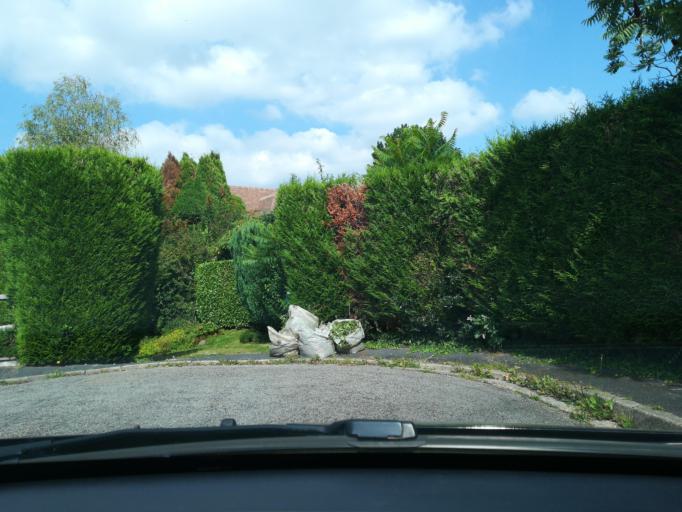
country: FR
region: Haute-Normandie
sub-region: Departement de la Seine-Maritime
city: Bois-Guillaume
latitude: 49.4768
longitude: 1.1188
